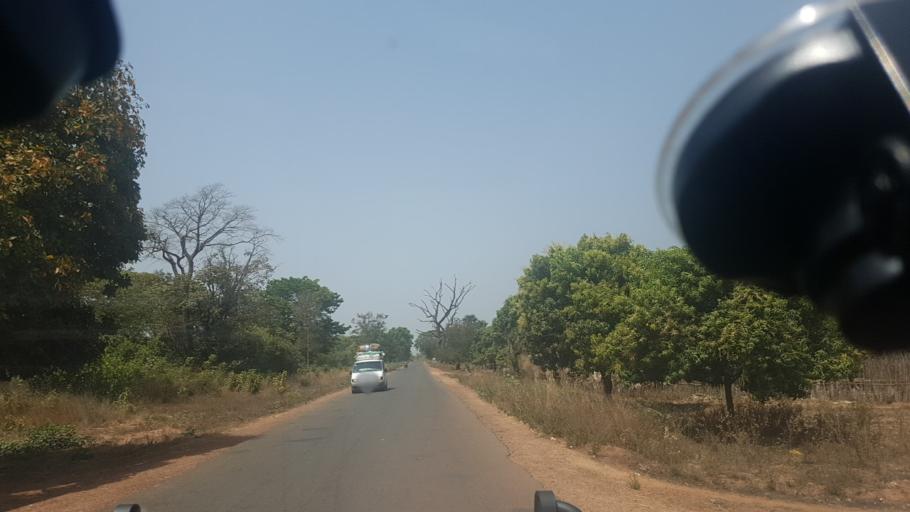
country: SN
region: Ziguinchor
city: Adeane
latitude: 12.3796
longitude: -15.7790
